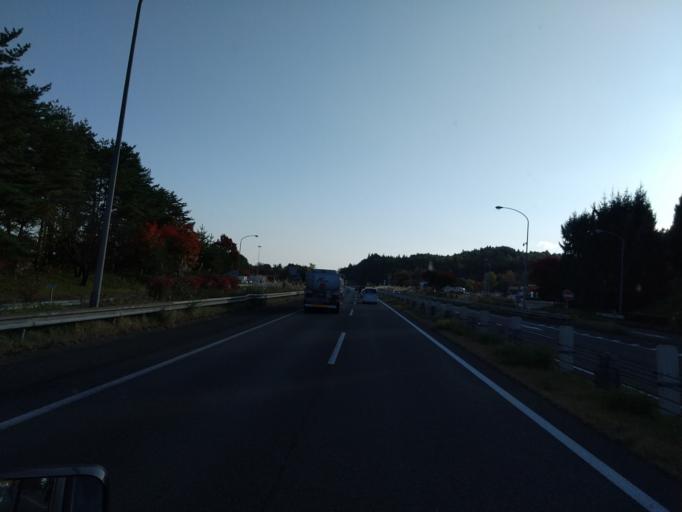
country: JP
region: Iwate
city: Hanamaki
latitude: 39.5172
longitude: 141.1030
